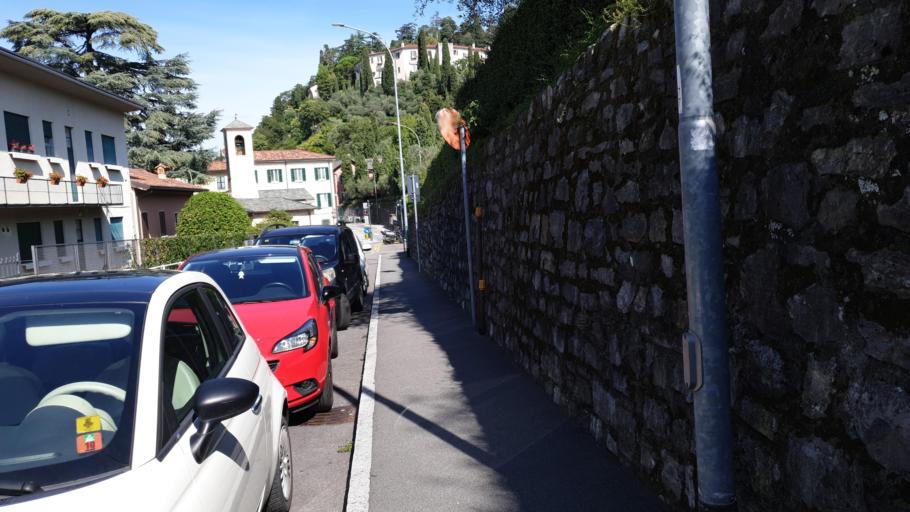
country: IT
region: Lombardy
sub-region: Provincia di Como
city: Bellagio
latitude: 45.9846
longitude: 9.2620
